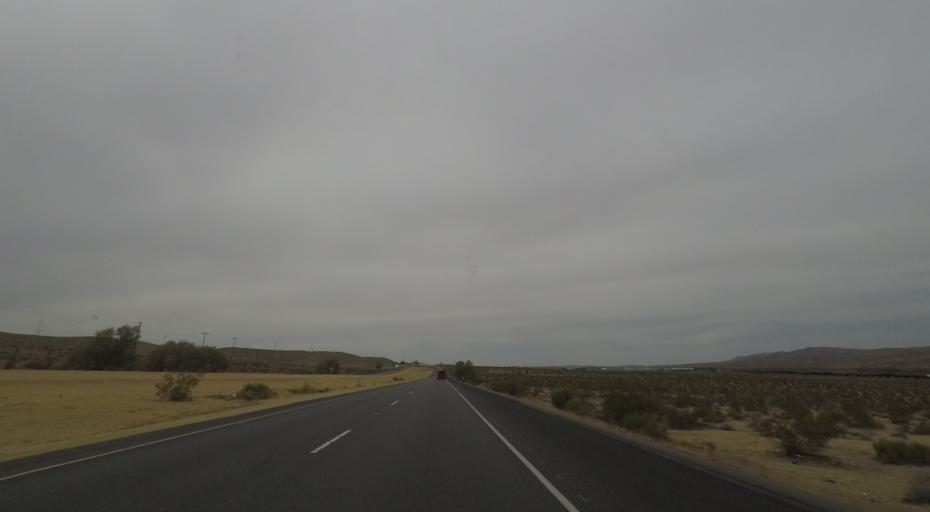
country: US
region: California
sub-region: San Bernardino County
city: Barstow
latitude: 34.8626
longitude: -116.9250
